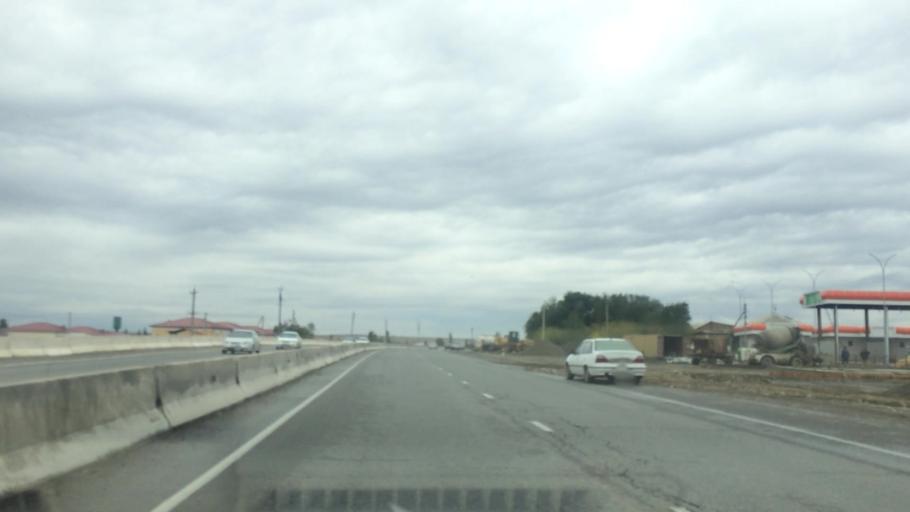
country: UZ
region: Jizzax
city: Jizzax
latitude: 39.9750
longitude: 67.5610
